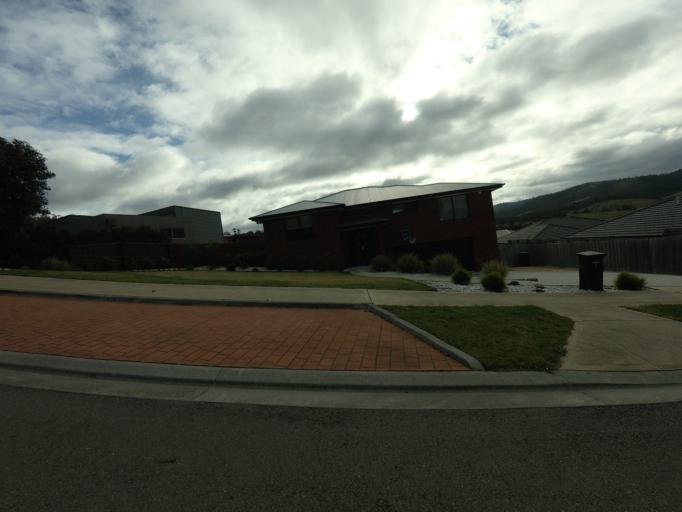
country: AU
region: Tasmania
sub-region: Clarence
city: Howrah
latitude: -42.8848
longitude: 147.4234
